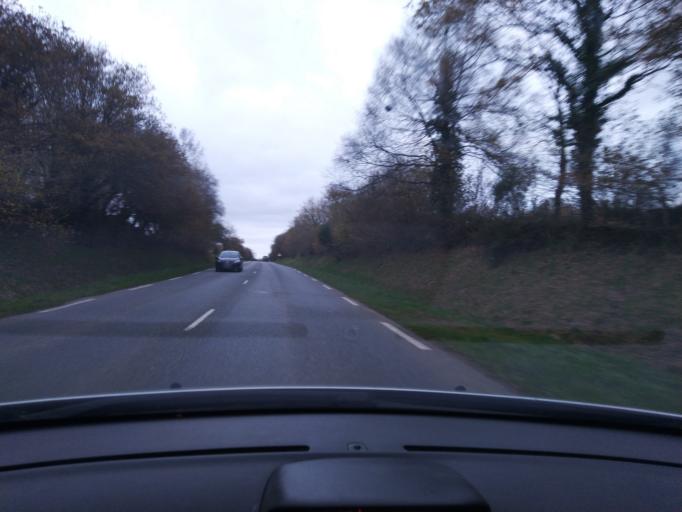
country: FR
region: Brittany
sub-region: Departement des Cotes-d'Armor
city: Plouaret
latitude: 48.5856
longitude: -3.4949
